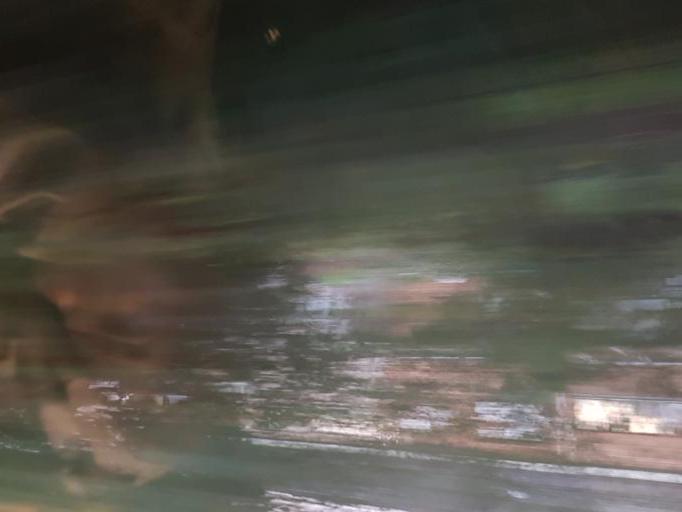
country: BE
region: Wallonia
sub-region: Province du Brabant Wallon
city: Braine-l'Alleud
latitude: 50.6890
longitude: 4.3765
